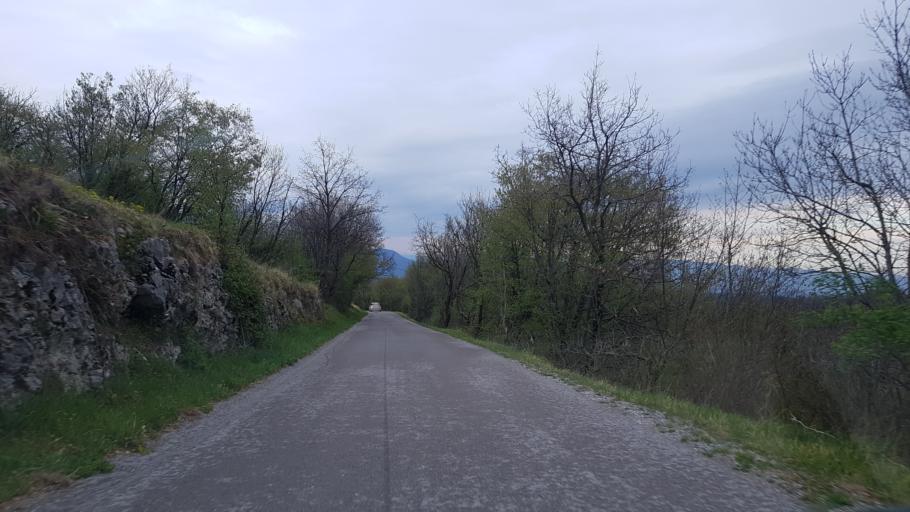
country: SI
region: Kanal
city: Deskle
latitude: 46.0421
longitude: 13.5644
